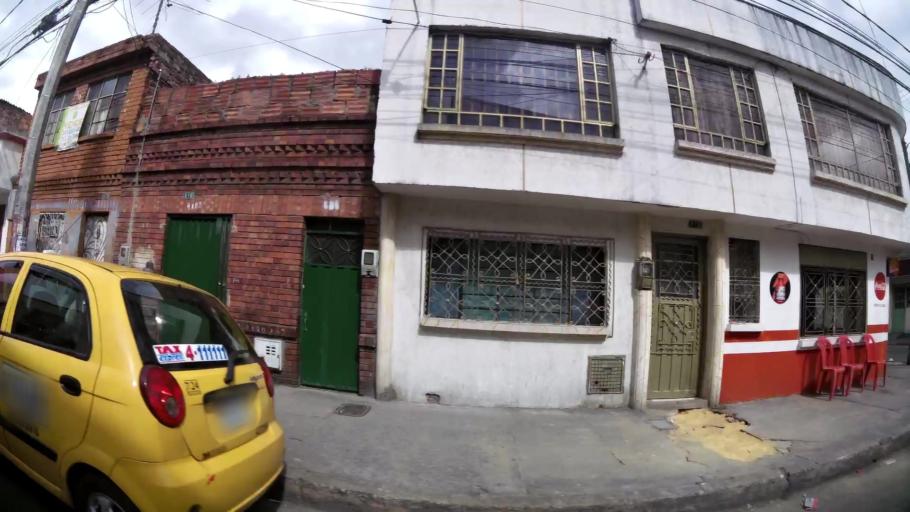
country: CO
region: Bogota D.C.
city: Bogota
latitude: 4.6259
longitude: -74.1200
